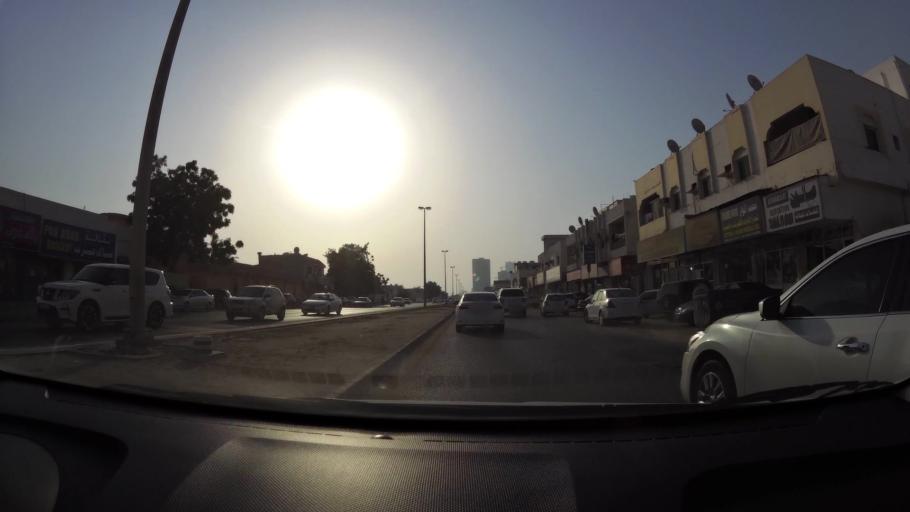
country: AE
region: Ajman
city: Ajman
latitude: 25.3821
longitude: 55.4471
